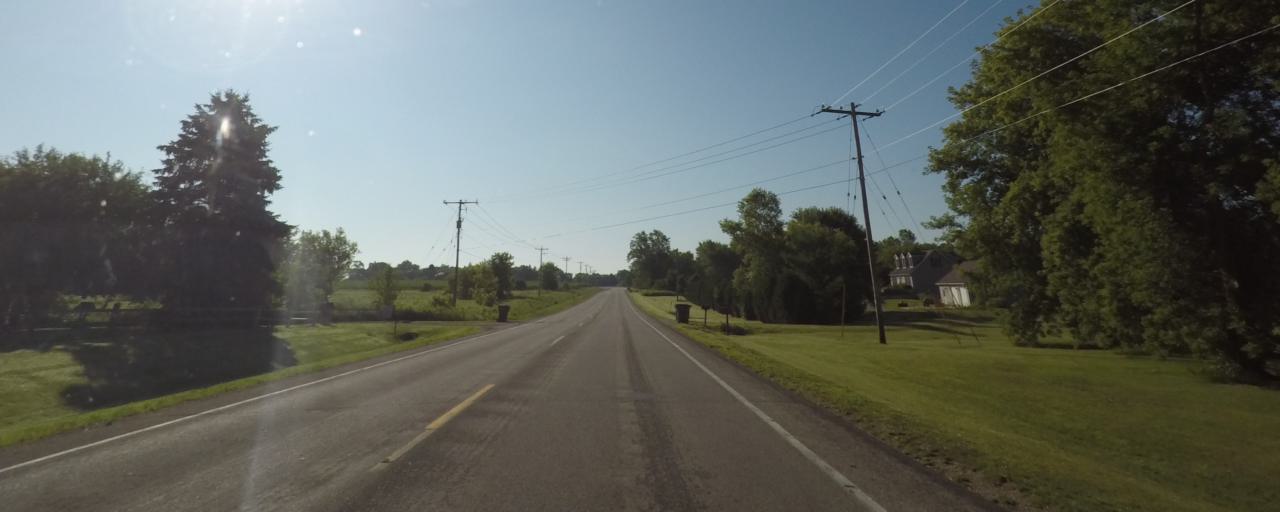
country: US
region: Wisconsin
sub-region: Walworth County
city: Whitewater
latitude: 42.9336
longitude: -88.7267
